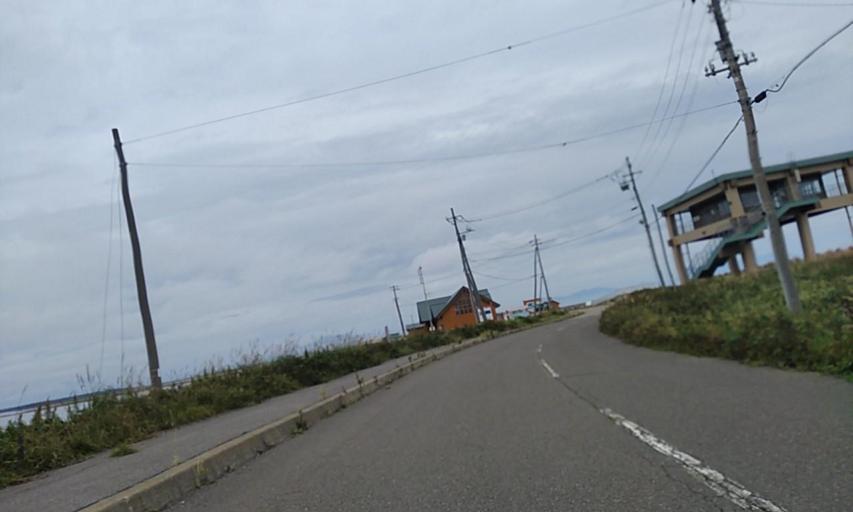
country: JP
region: Hokkaido
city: Shibetsu
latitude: 43.5892
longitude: 145.3361
